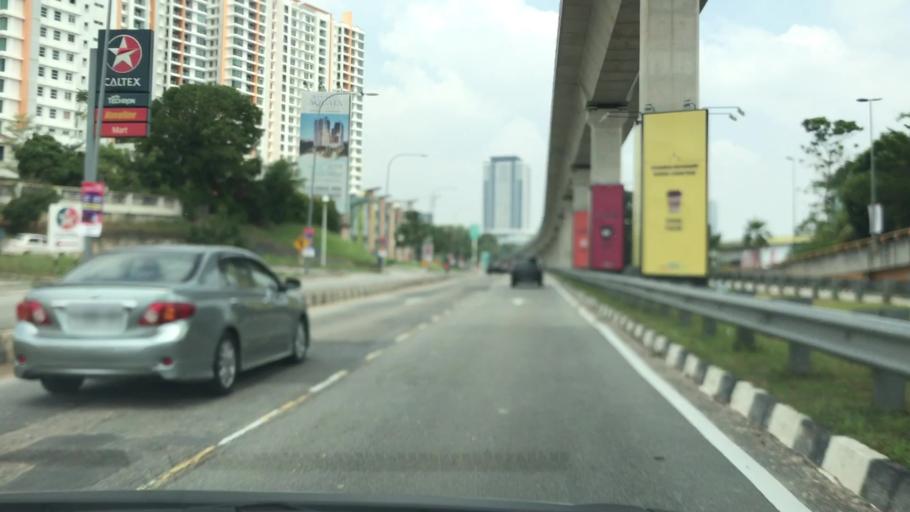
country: MY
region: Selangor
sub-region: Petaling
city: Petaling Jaya
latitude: 3.0540
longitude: 101.6551
